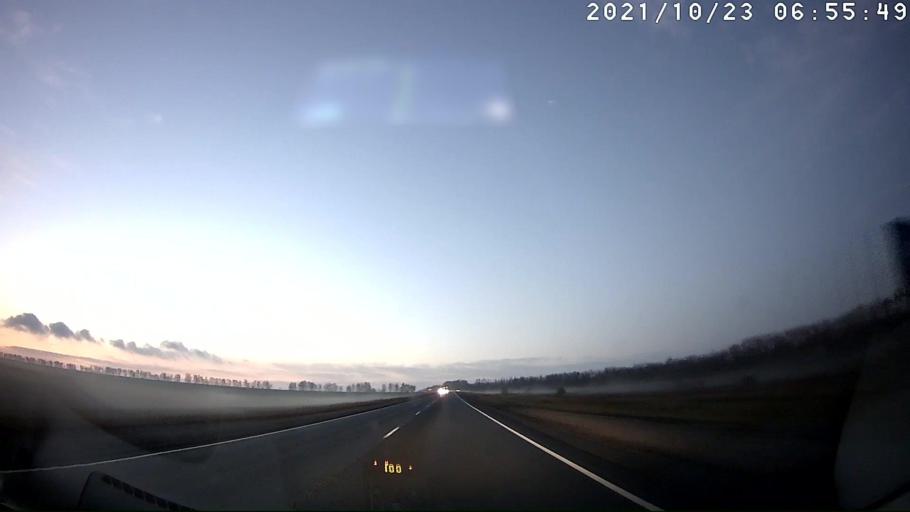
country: RU
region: Saratov
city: Dukhovnitskoye
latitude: 52.7322
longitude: 48.2578
